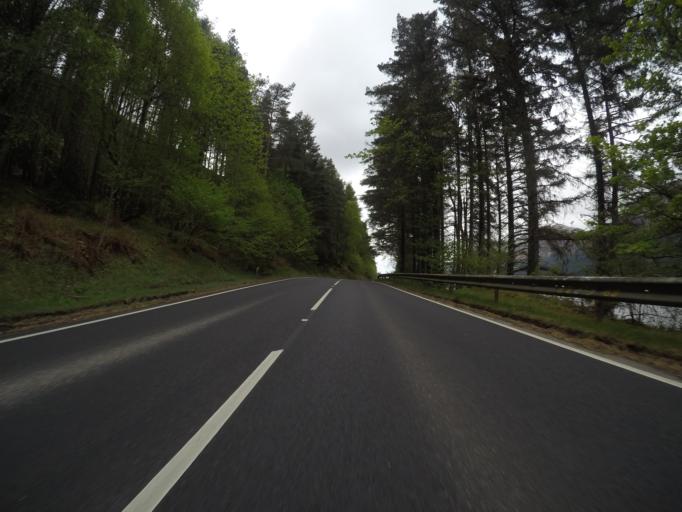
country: GB
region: Scotland
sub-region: Highland
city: Spean Bridge
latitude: 57.0097
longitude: -4.8387
